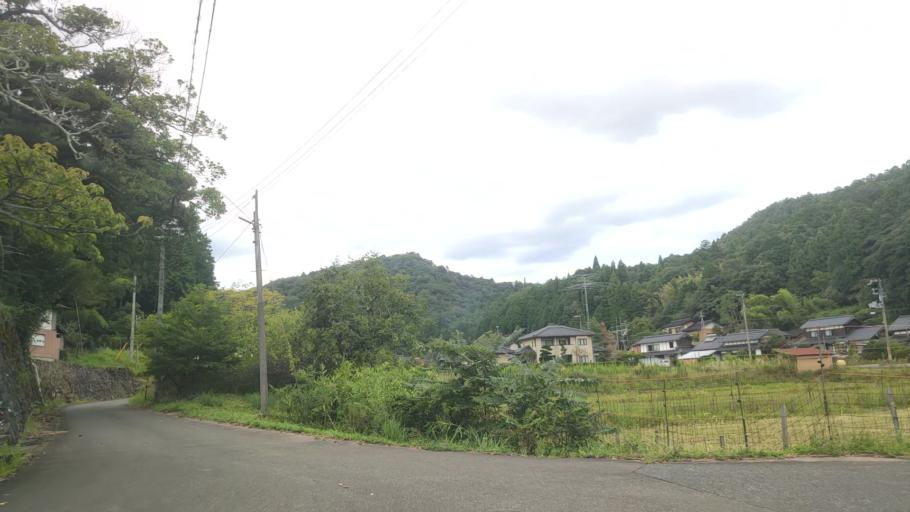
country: JP
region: Hyogo
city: Toyooka
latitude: 35.5987
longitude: 134.8818
